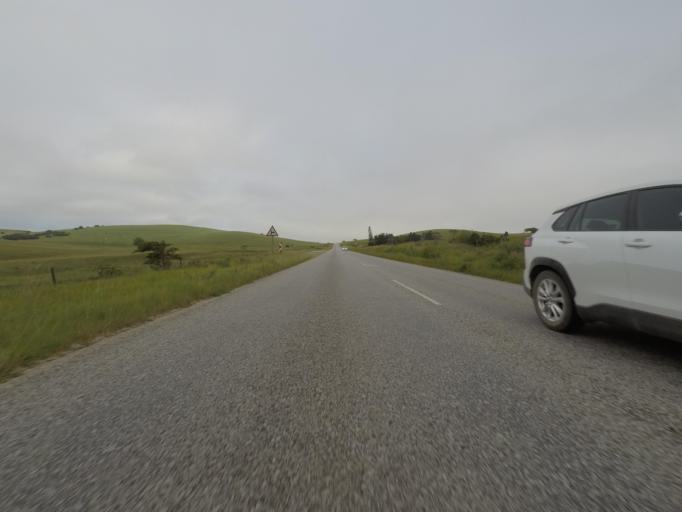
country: ZA
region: Eastern Cape
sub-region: Cacadu District Municipality
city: Port Alfred
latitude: -33.6089
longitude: 26.8136
